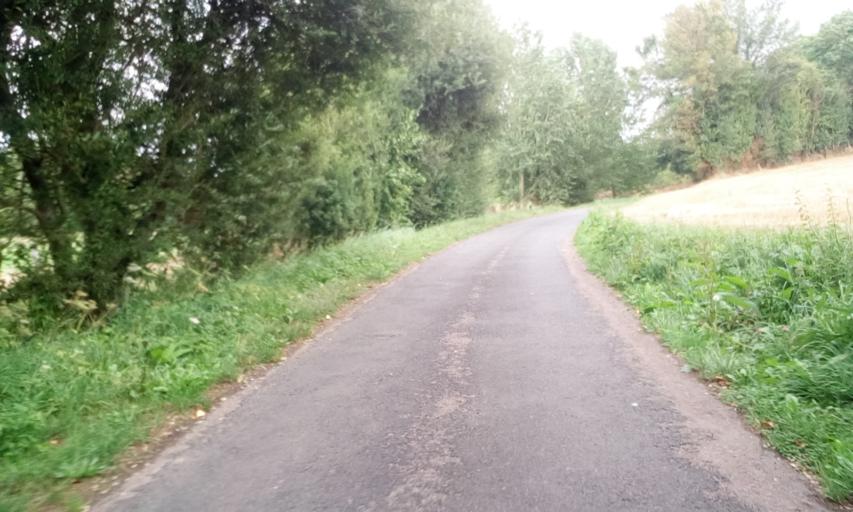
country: FR
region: Lower Normandy
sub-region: Departement du Calvados
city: Tilly-sur-Seulles
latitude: 49.2096
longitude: -0.6232
